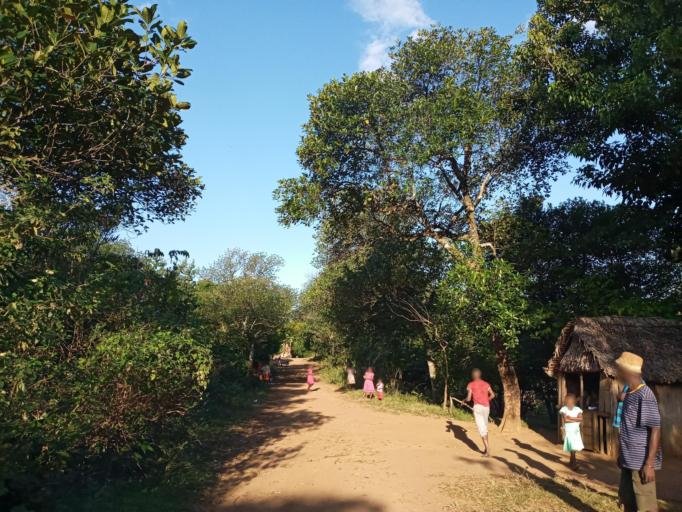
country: MG
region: Anosy
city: Fort Dauphin
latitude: -24.8060
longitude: 47.0801
